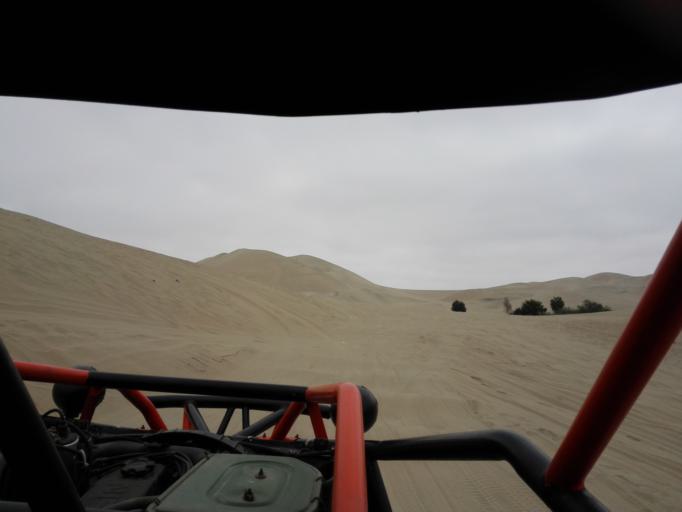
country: PE
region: Ica
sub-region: Provincia de Ica
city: Ica
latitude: -14.0890
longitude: -75.7649
